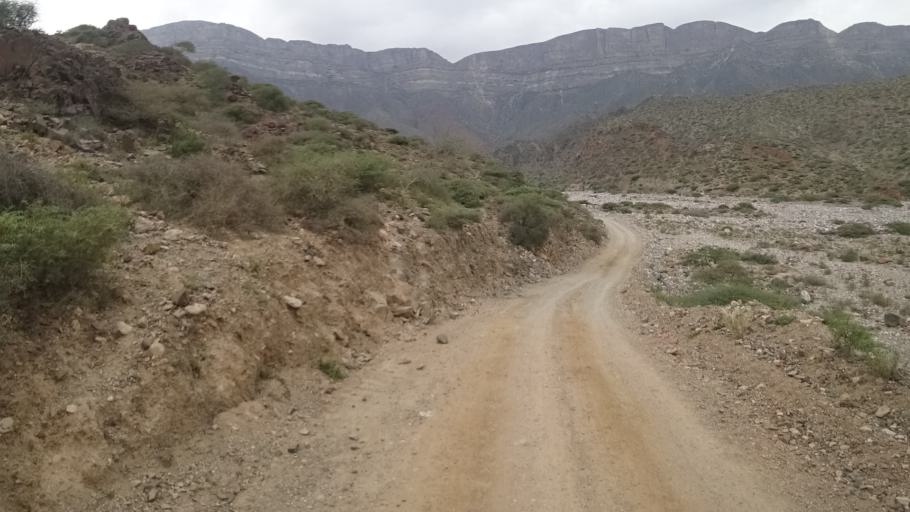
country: OM
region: Zufar
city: Salalah
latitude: 17.1755
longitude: 54.9503
